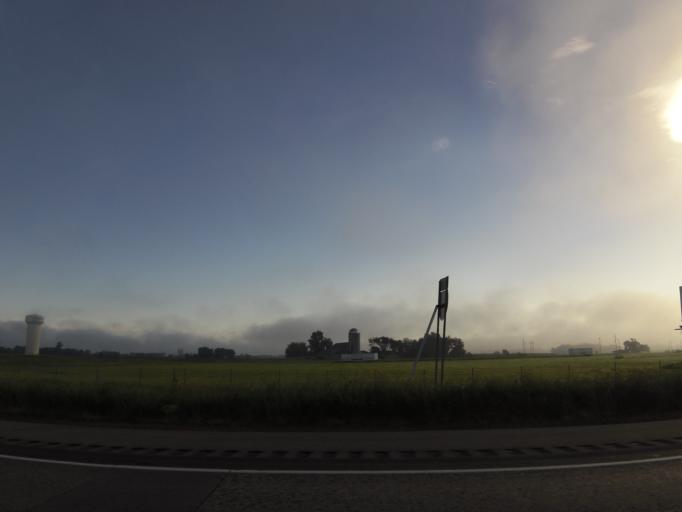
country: US
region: Minnesota
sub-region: Wright County
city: Albertville
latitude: 45.2466
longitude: -93.6780
